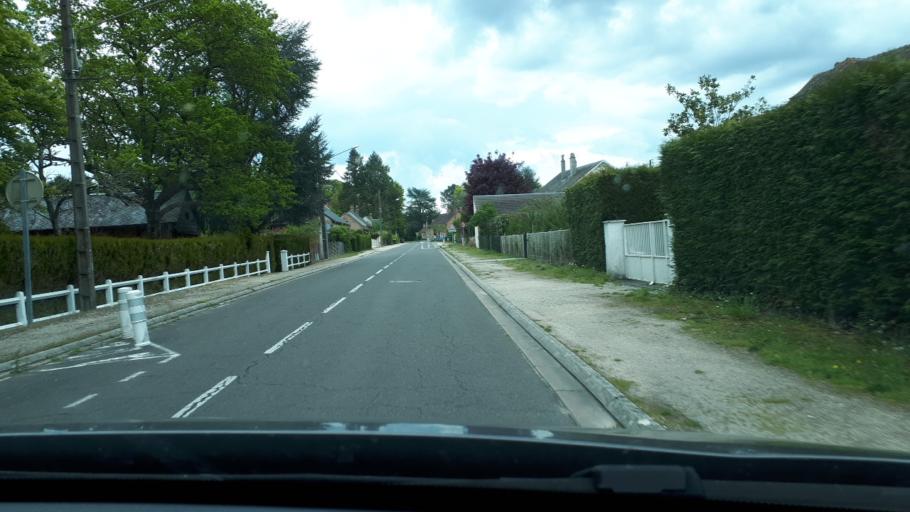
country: FR
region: Centre
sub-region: Departement du Loir-et-Cher
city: Nouan-le-Fuzelier
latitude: 47.5354
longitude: 2.0424
